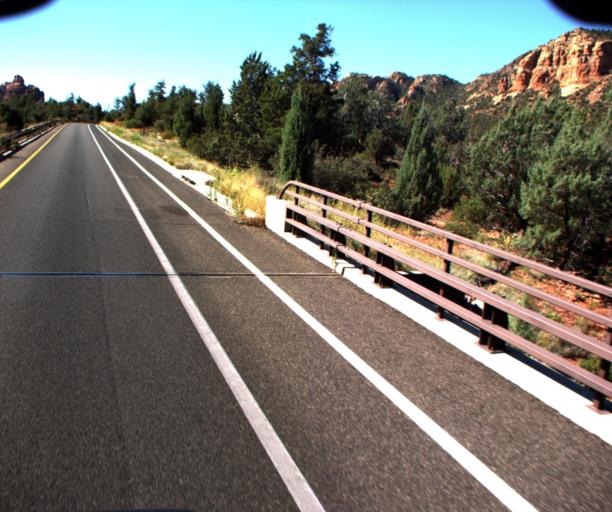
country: US
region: Arizona
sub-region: Yavapai County
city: Village of Oak Creek (Big Park)
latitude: 34.8147
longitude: -111.7691
